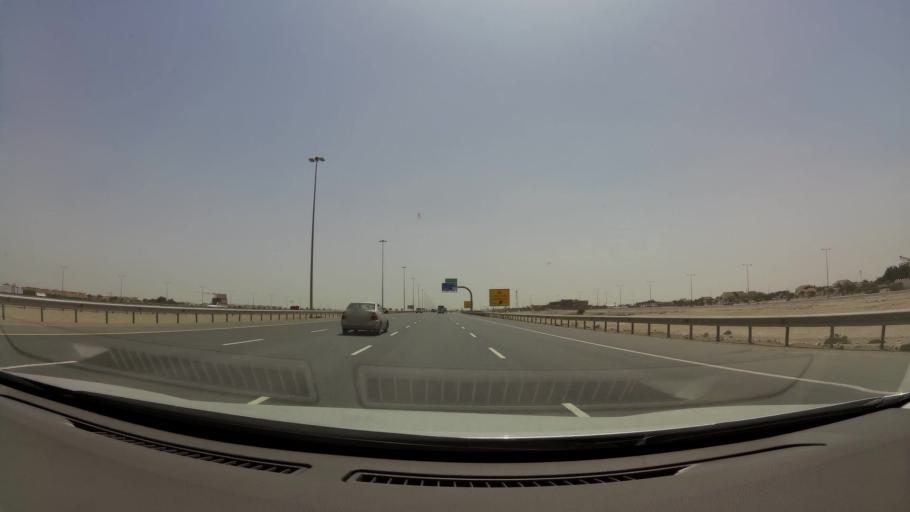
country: QA
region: Baladiyat Umm Salal
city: Umm Salal `Ali
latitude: 25.4638
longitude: 51.4084
